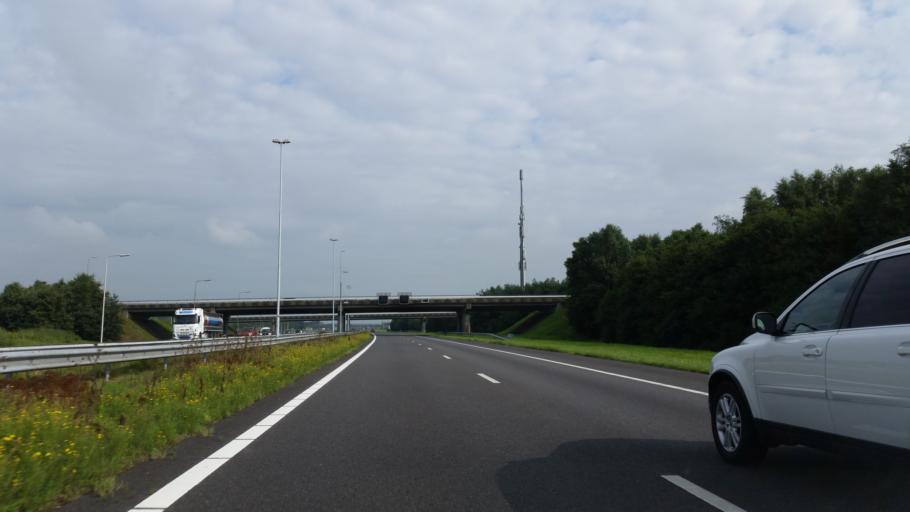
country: NL
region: North Brabant
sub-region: Gemeente Breda
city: Breda
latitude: 51.5241
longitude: 4.7451
